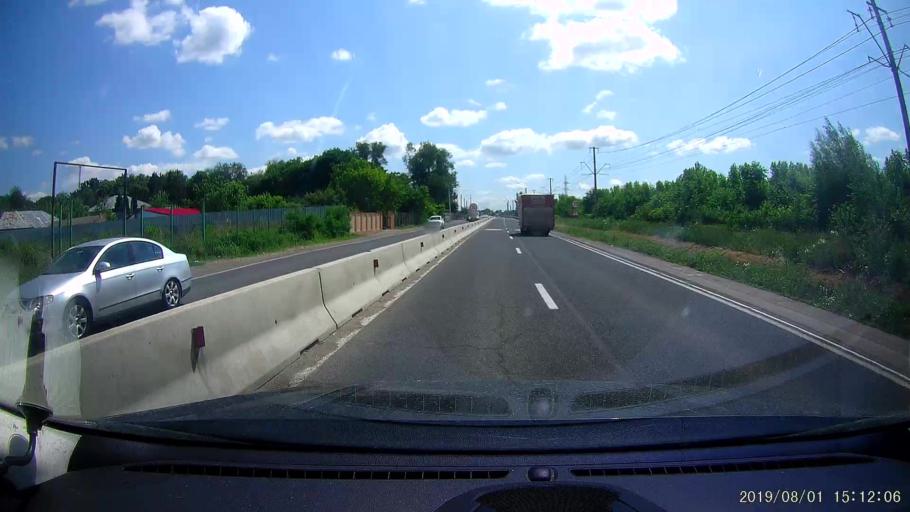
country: RO
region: Braila
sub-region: Comuna Chiscani
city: Lacu Sarat
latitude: 45.2095
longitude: 27.9168
